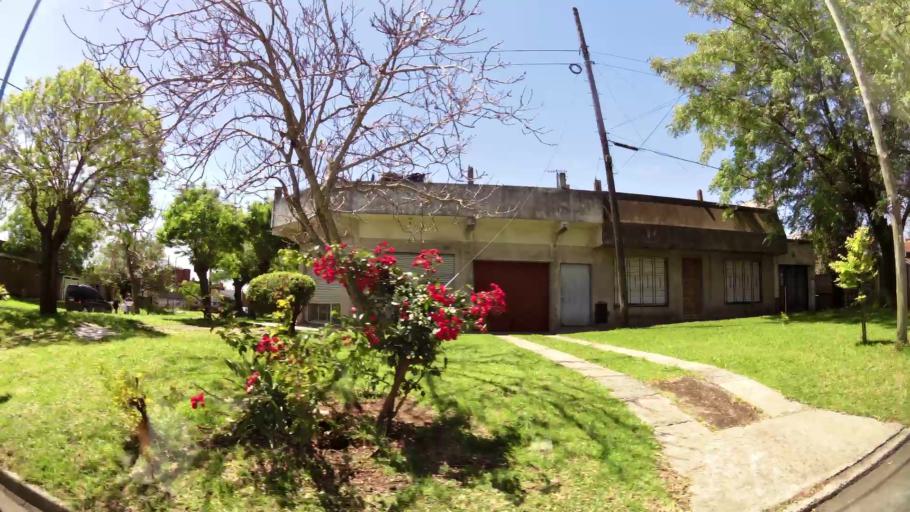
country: AR
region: Buenos Aires
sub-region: Partido de Quilmes
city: Quilmes
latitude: -34.7360
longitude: -58.2808
